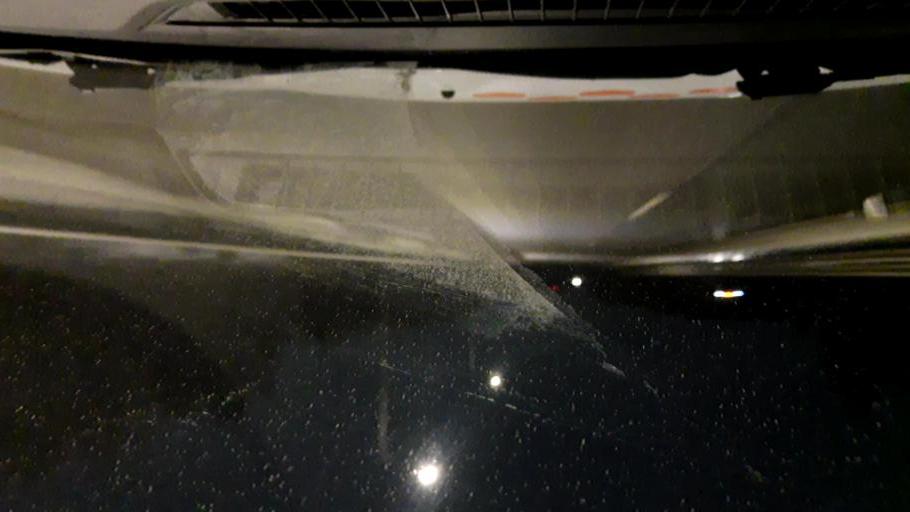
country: RU
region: Nizjnij Novgorod
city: Burevestnik
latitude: 56.1418
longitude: 43.7596
